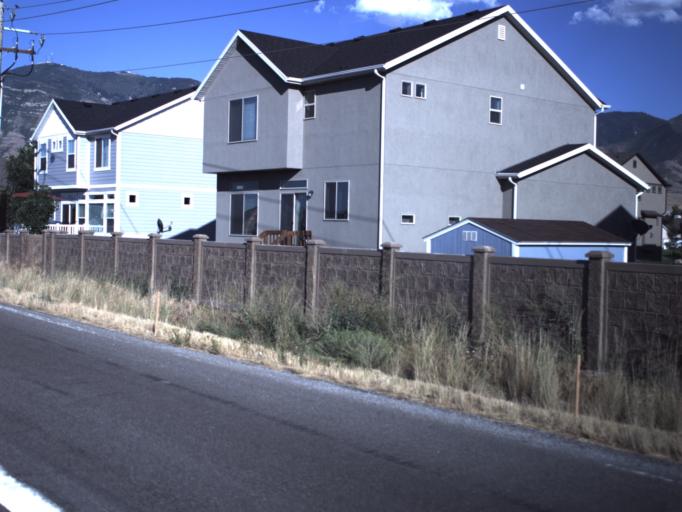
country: US
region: Utah
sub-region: Tooele County
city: Stansbury park
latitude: 40.6466
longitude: -112.3038
